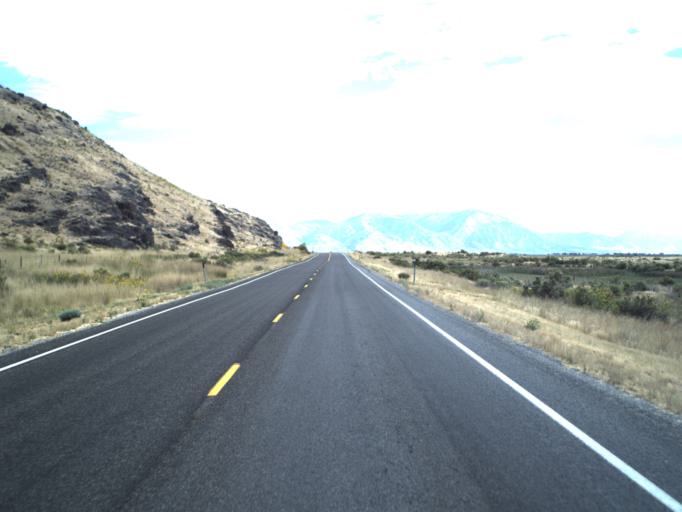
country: US
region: Utah
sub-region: Box Elder County
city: Elwood
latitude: 41.5817
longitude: -112.2567
